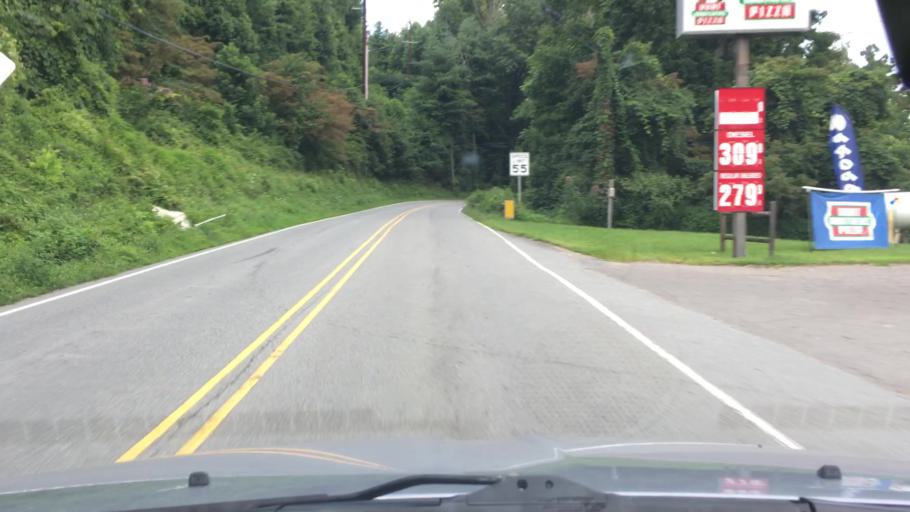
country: US
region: North Carolina
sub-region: Yancey County
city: Burnsville
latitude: 35.8605
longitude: -82.1992
